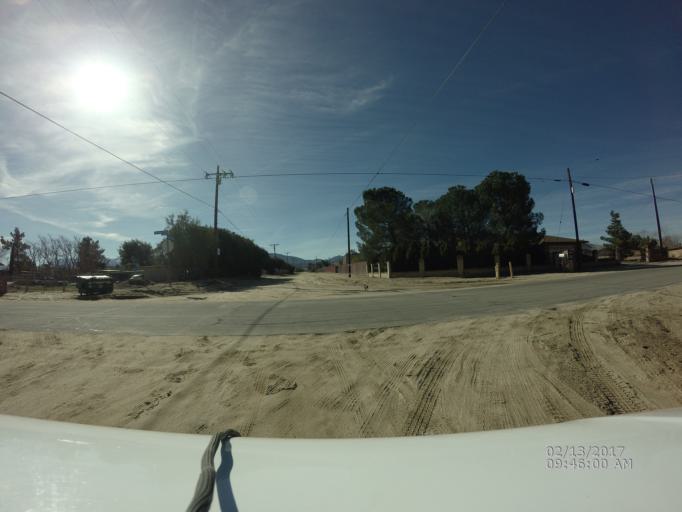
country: US
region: California
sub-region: Los Angeles County
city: Littlerock
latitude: 34.5357
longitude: -117.9669
